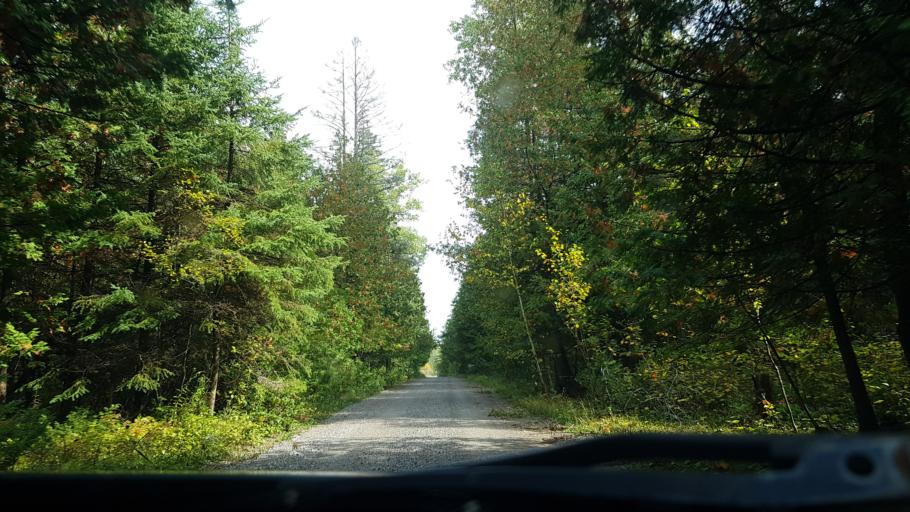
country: CA
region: Ontario
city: Orillia
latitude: 44.6795
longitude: -79.0734
